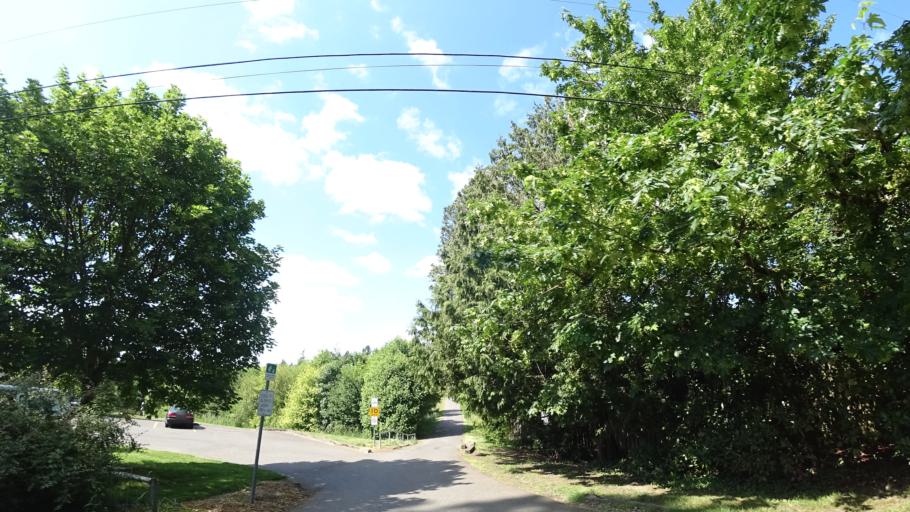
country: US
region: Oregon
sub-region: Washington County
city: Garden Home-Whitford
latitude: 45.4690
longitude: -122.7195
